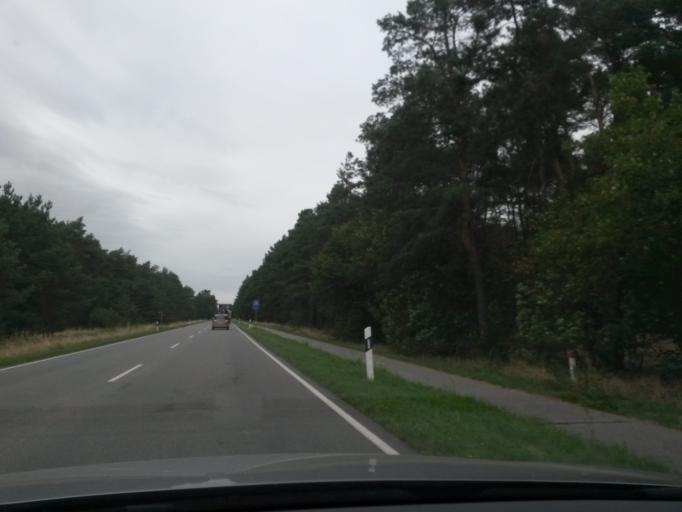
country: DE
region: Saxony-Anhalt
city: Klietz
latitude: 52.6837
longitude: 12.0659
